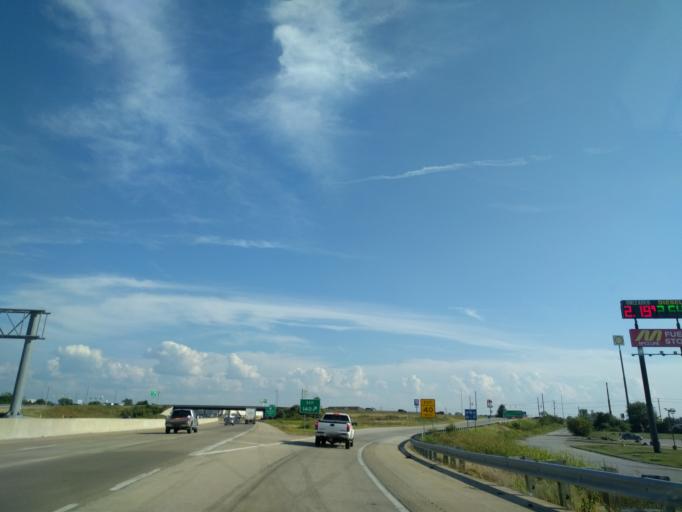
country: US
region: Indiana
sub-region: Boone County
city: Lebanon
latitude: 40.0490
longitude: -86.4912
